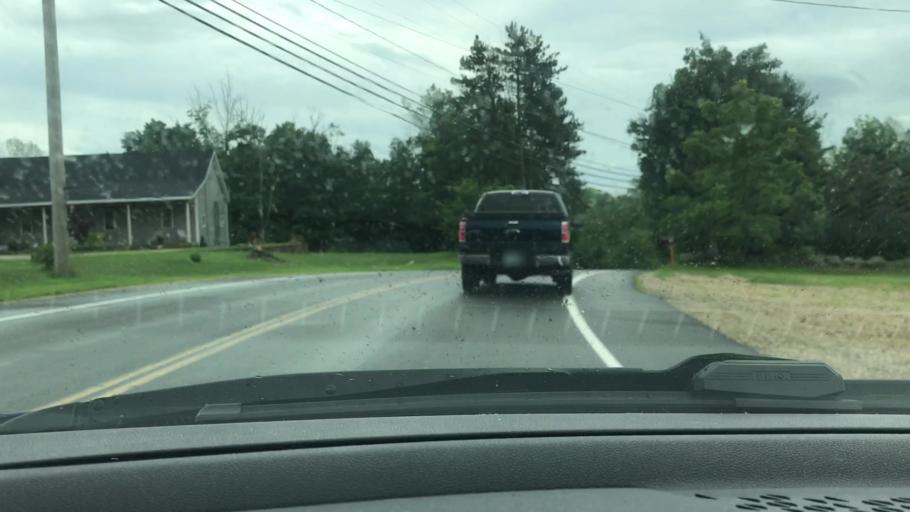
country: US
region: New Hampshire
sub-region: Rockingham County
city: Candia
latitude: 43.1356
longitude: -71.2390
